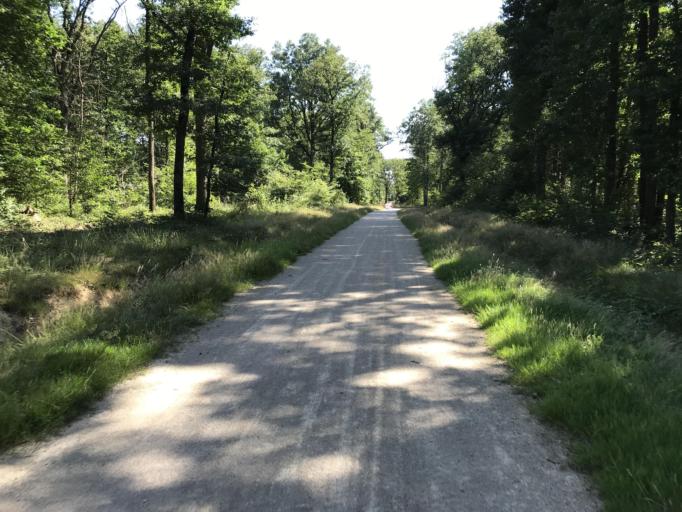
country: FR
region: Ile-de-France
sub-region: Departement de l'Essonne
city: Bondoufle
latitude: 48.6325
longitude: 2.3847
